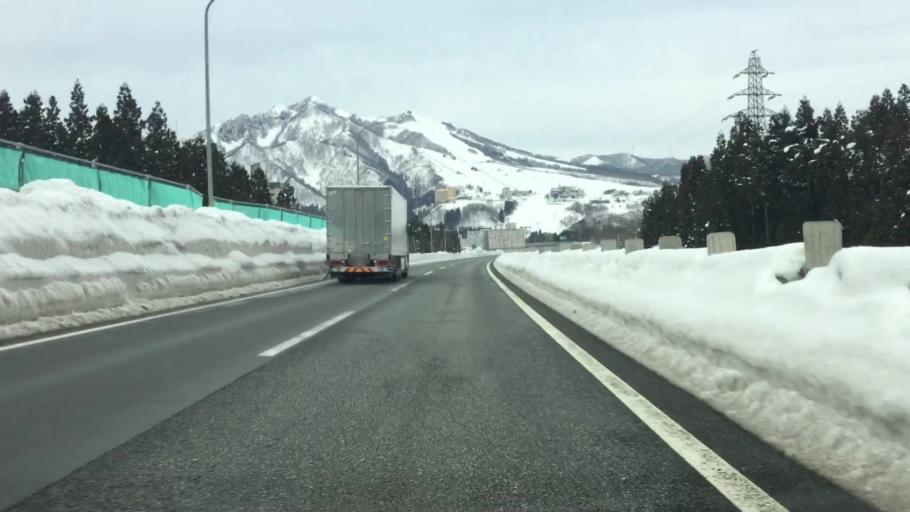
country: JP
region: Niigata
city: Shiozawa
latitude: 36.9144
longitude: 138.8395
